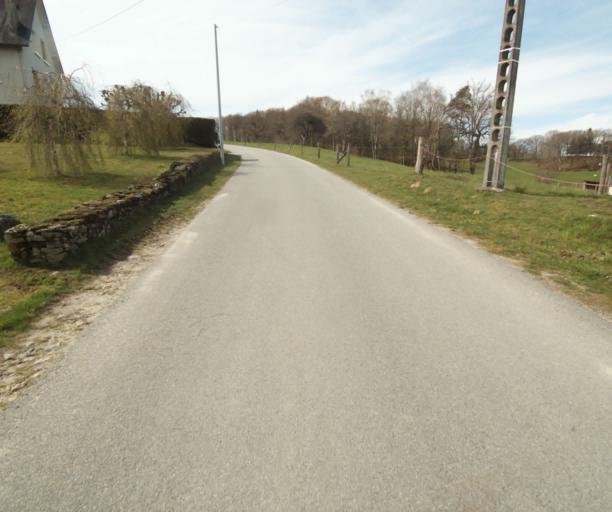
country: FR
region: Limousin
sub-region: Departement de la Correze
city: Correze
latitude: 45.3647
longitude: 1.8854
